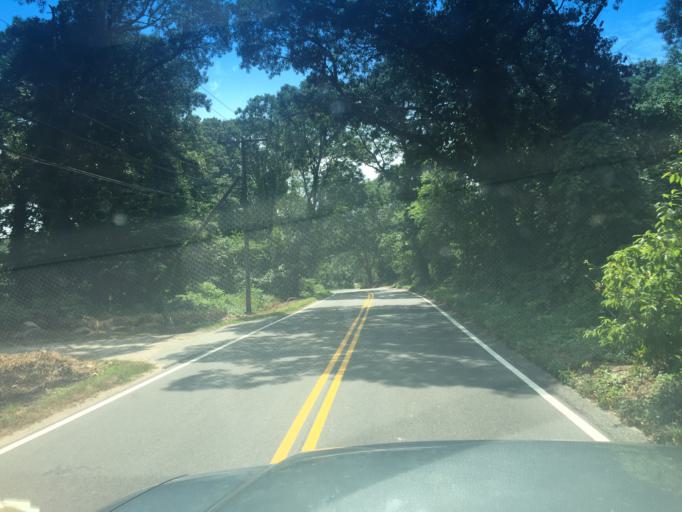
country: US
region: Massachusetts
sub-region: Barnstable County
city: West Falmouth
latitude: 41.5804
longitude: -70.6285
